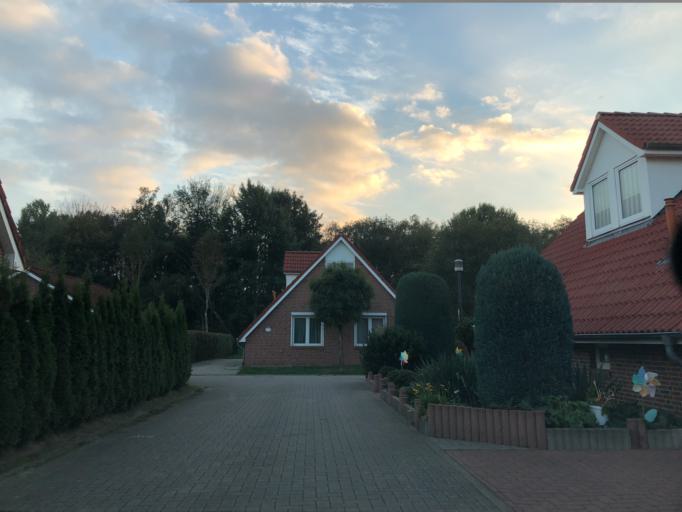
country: DE
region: Lower Saxony
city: Papenburg
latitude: 53.0651
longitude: 7.4343
